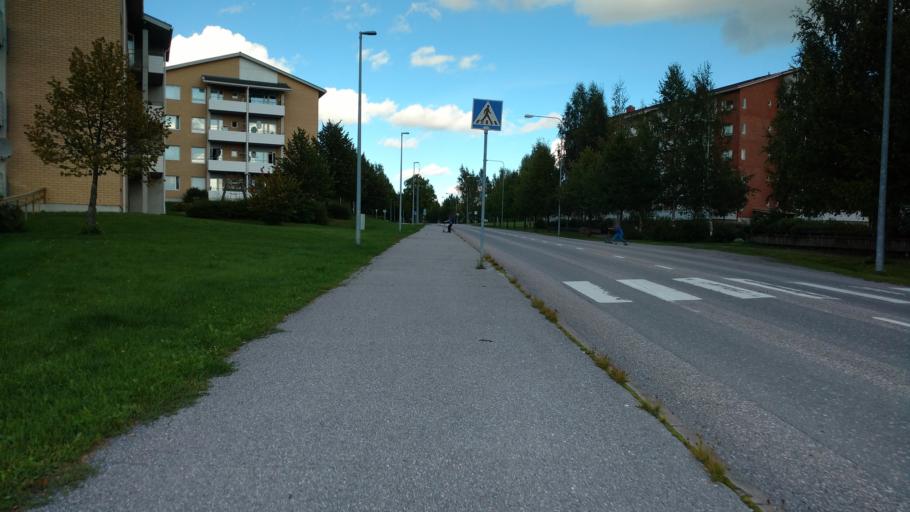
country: FI
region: Varsinais-Suomi
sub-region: Salo
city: Salo
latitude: 60.3813
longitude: 23.1529
